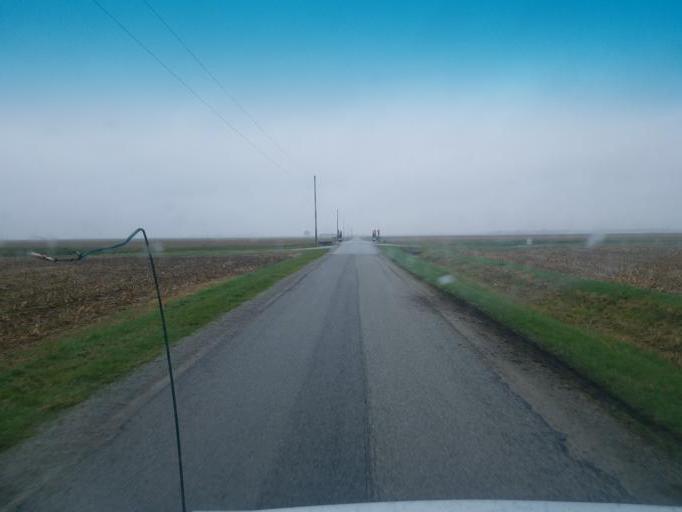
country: US
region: Ohio
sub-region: Wood County
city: North Baltimore
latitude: 41.2685
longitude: -83.6402
